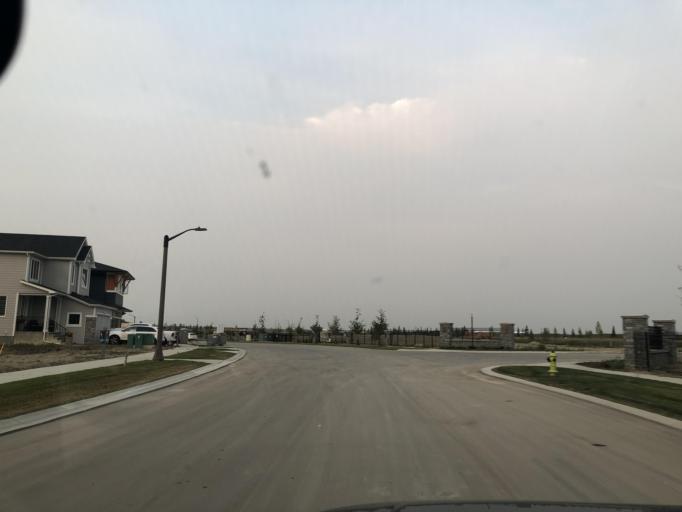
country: CA
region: Alberta
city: Cochrane
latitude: 51.1191
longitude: -114.3933
